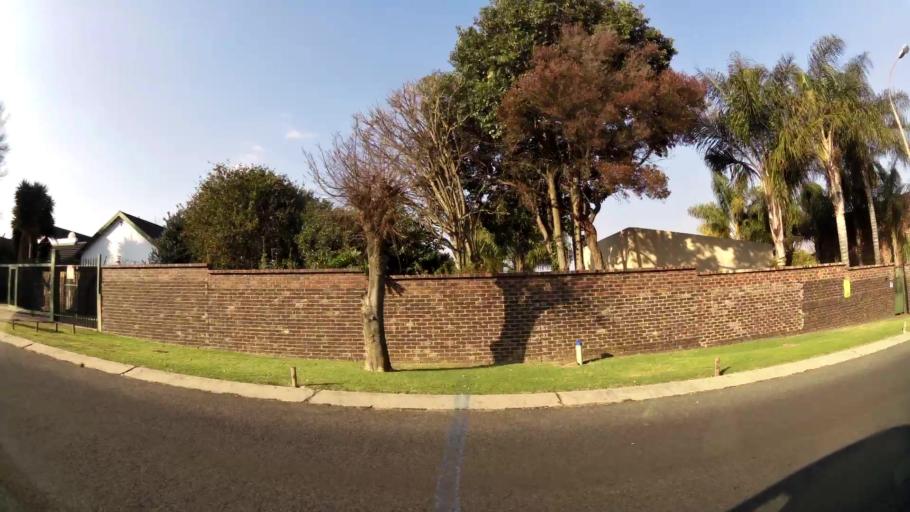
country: ZA
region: Gauteng
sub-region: City of Johannesburg Metropolitan Municipality
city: Modderfontein
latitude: -26.0811
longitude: 28.2056
